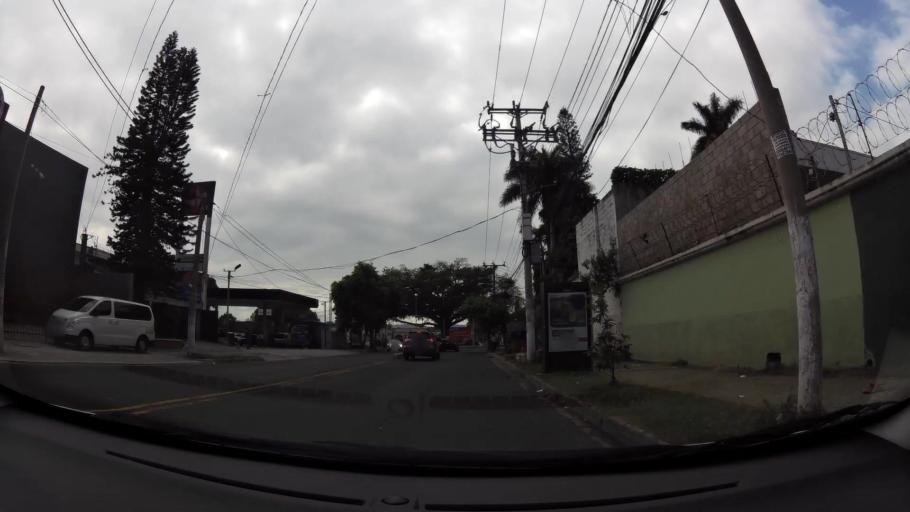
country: SV
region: San Salvador
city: Mejicanos
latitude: 13.7127
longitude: -89.2477
